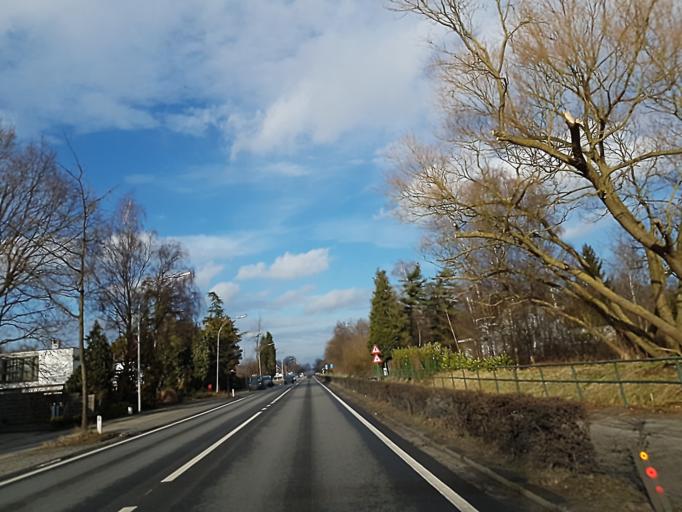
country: BE
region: Flanders
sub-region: Provincie Antwerpen
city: Mol
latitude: 51.2125
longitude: 5.1153
